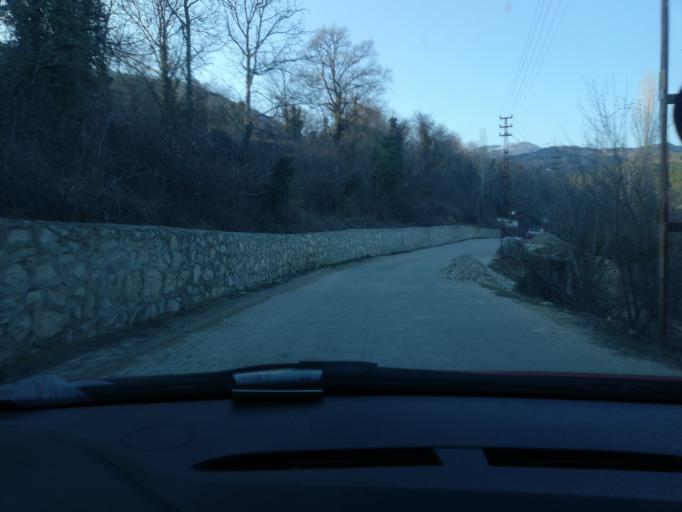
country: TR
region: Karabuk
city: Safranbolu
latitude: 41.2842
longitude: 32.6782
